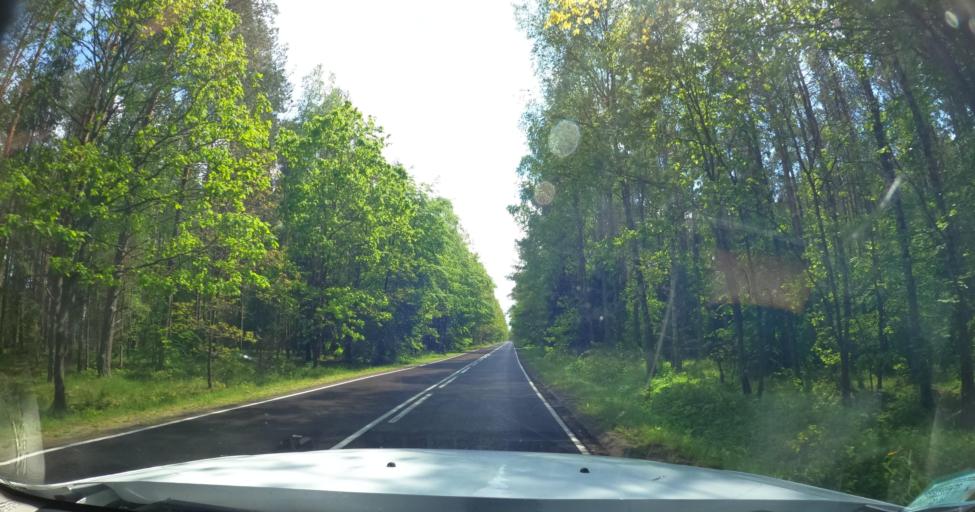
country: PL
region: Pomeranian Voivodeship
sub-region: Powiat slupski
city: Potegowo
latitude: 54.3966
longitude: 17.4683
